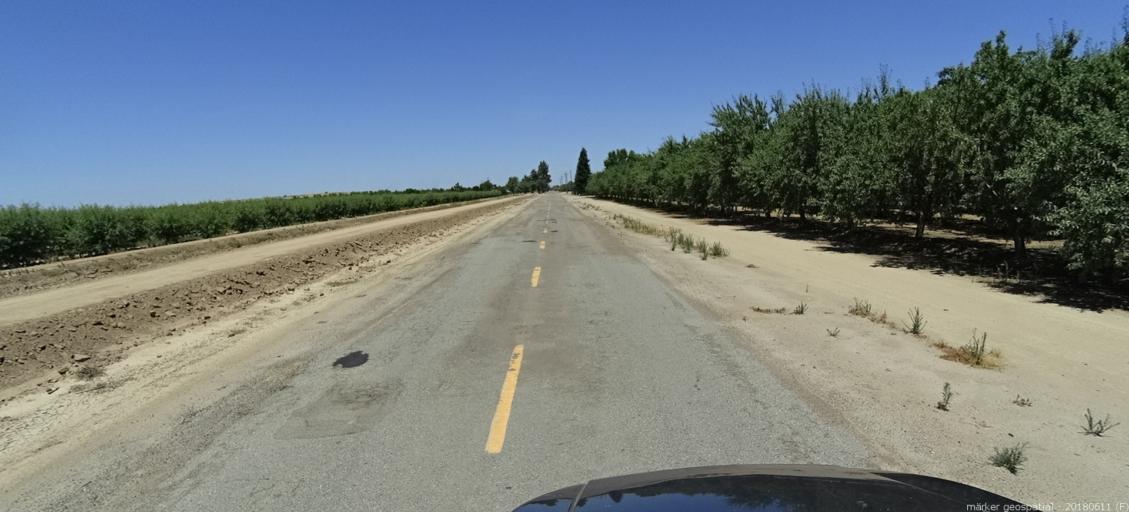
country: US
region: California
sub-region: Madera County
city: Fairmead
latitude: 37.0557
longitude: -120.1934
